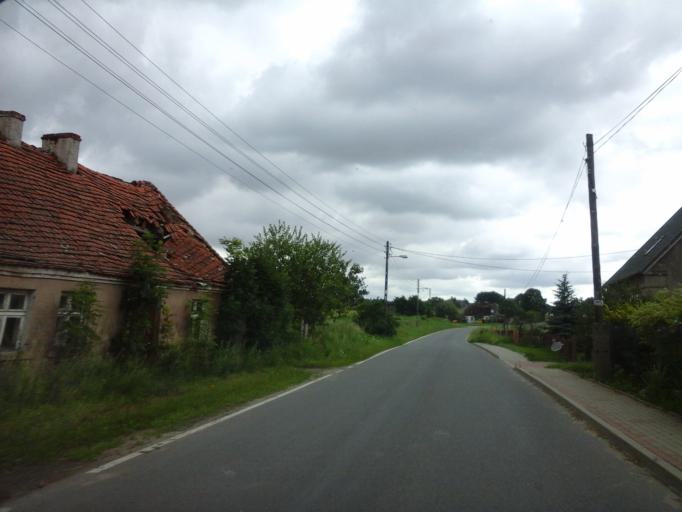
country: PL
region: West Pomeranian Voivodeship
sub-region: Powiat choszczenski
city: Krzecin
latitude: 53.0002
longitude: 15.4238
